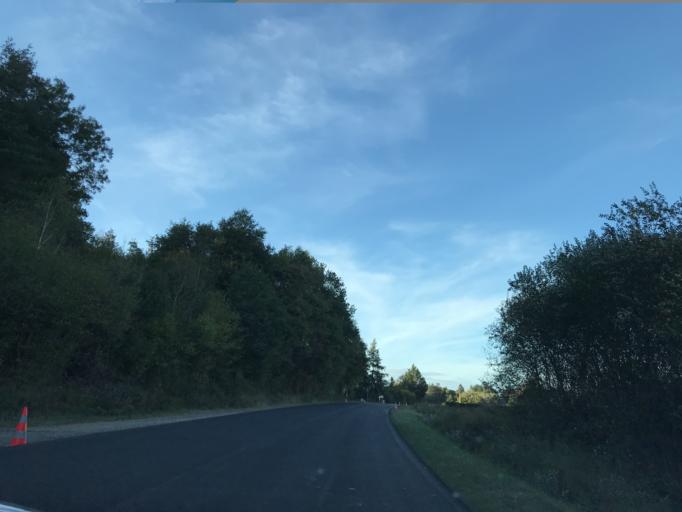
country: FR
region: Auvergne
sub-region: Departement du Puy-de-Dome
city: Paslieres
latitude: 45.8926
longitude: 3.5191
